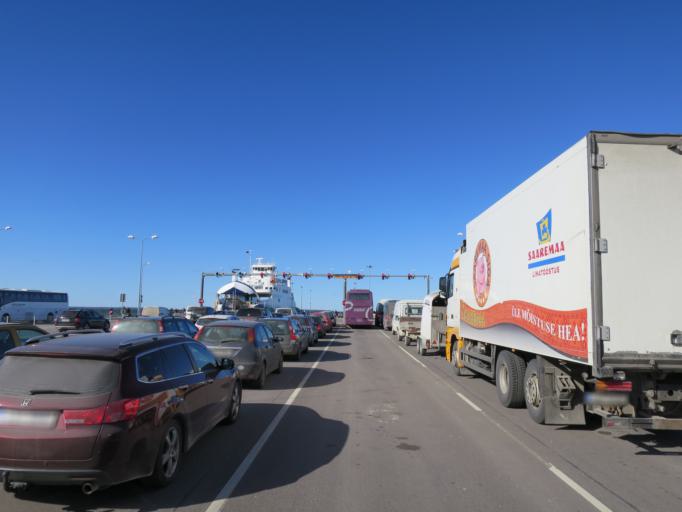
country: EE
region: Laeaene
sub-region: Lihula vald
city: Lihula
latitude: 58.5740
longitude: 23.5101
